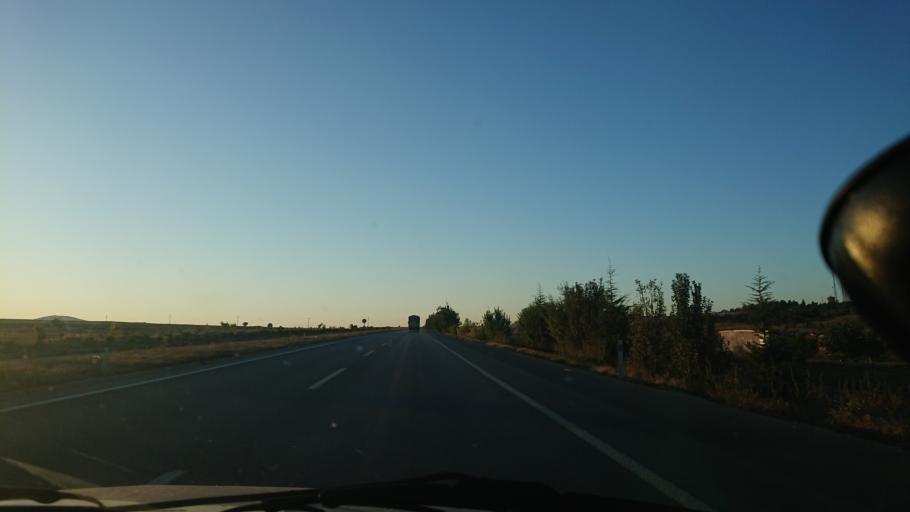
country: TR
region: Eskisehir
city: Mahmudiye
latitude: 39.4925
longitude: 30.9765
